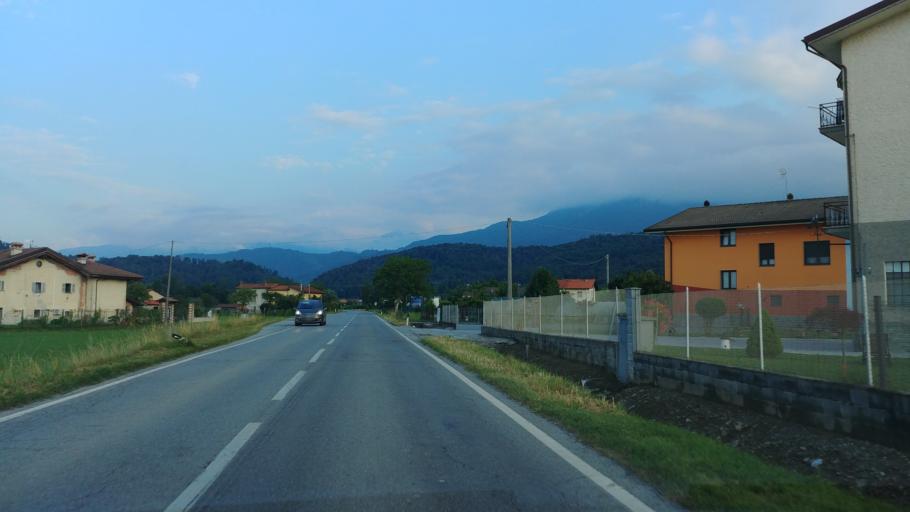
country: IT
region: Piedmont
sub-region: Provincia di Cuneo
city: Peveragno
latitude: 44.3425
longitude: 7.5979
